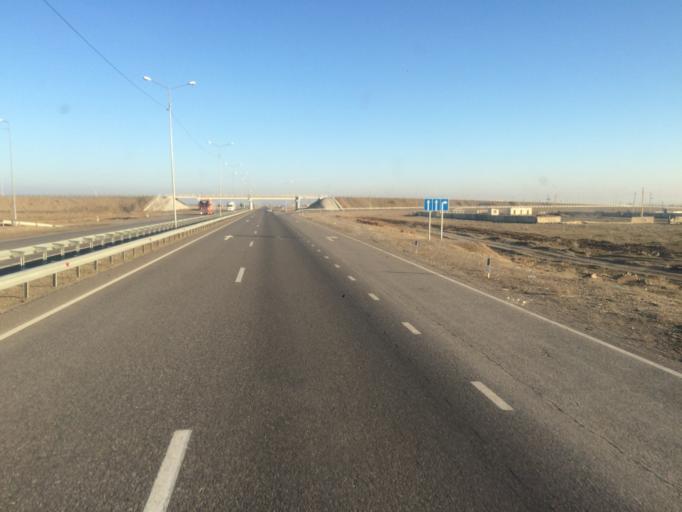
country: KZ
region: Ongtustik Qazaqstan
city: Turkestan
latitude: 43.4163
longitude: 68.0214
